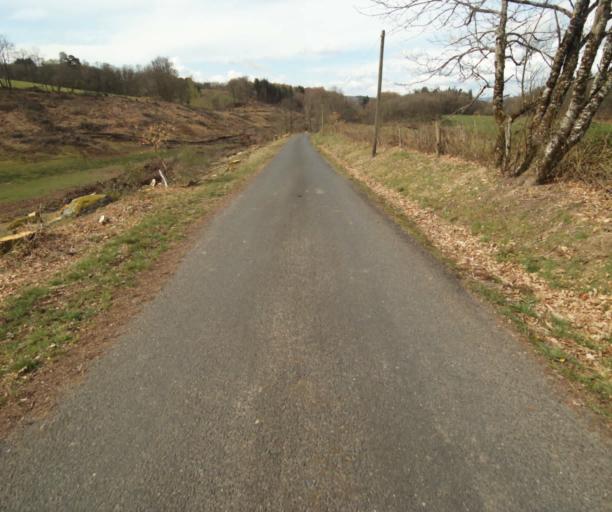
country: FR
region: Limousin
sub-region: Departement de la Correze
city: Correze
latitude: 45.3690
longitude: 1.9154
